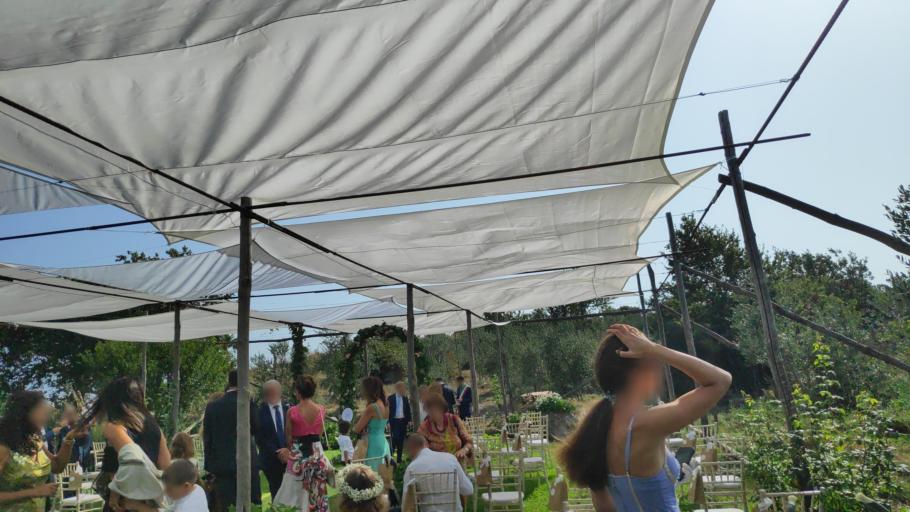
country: IT
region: Campania
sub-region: Provincia di Napoli
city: Massa Lubrense
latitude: 40.6047
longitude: 14.3850
